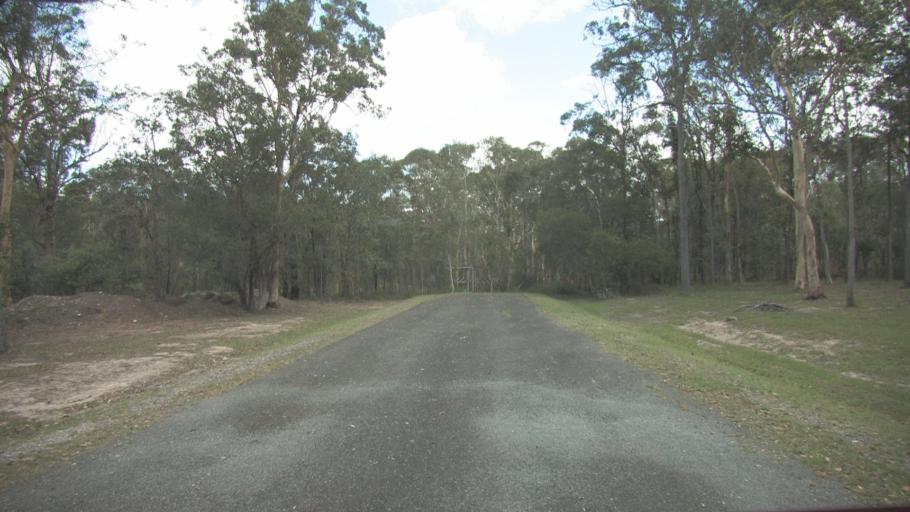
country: AU
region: Queensland
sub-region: Redland
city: Redland Bay
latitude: -27.6511
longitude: 153.2432
